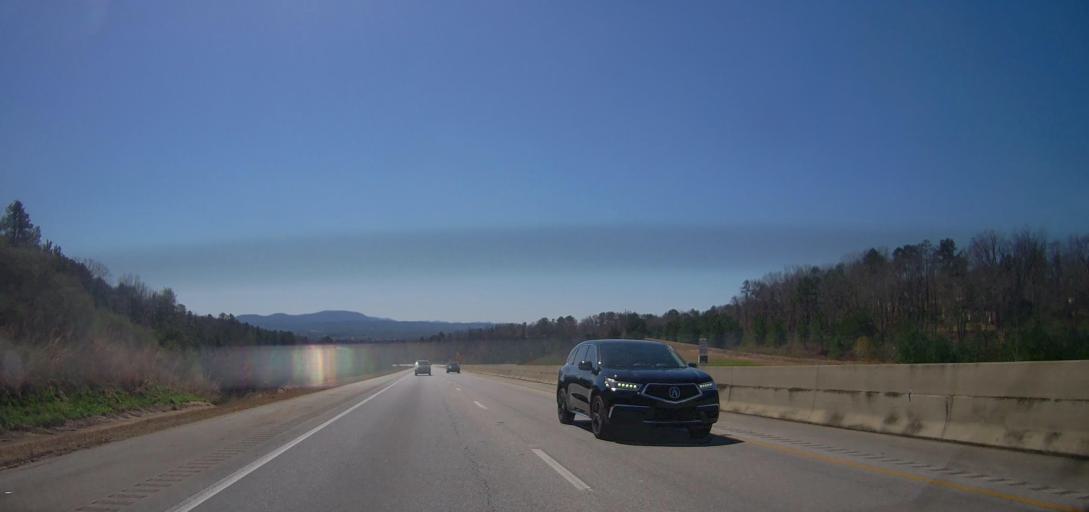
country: US
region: Alabama
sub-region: Calhoun County
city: Anniston
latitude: 33.6540
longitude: -85.7848
